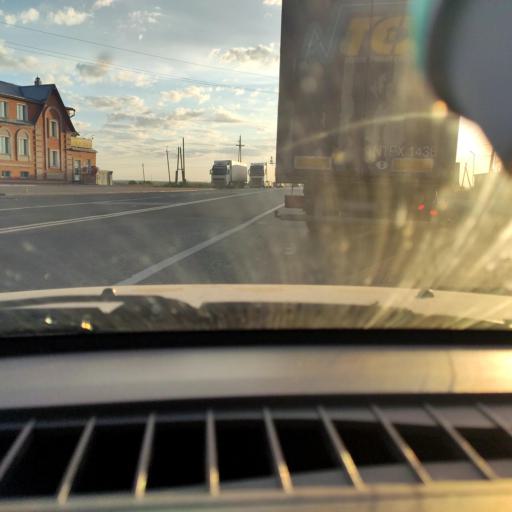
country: RU
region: Kirov
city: Kotel'nich
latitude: 58.3192
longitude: 48.3975
